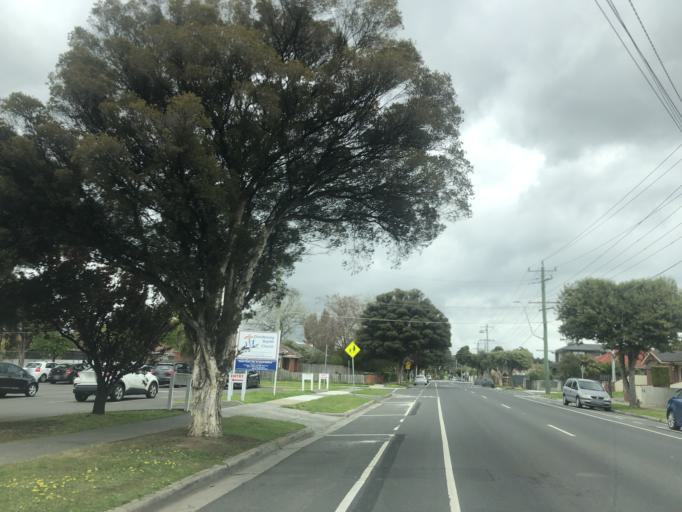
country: AU
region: Victoria
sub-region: Greater Dandenong
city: Dandenong North
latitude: -37.9747
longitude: 145.2103
